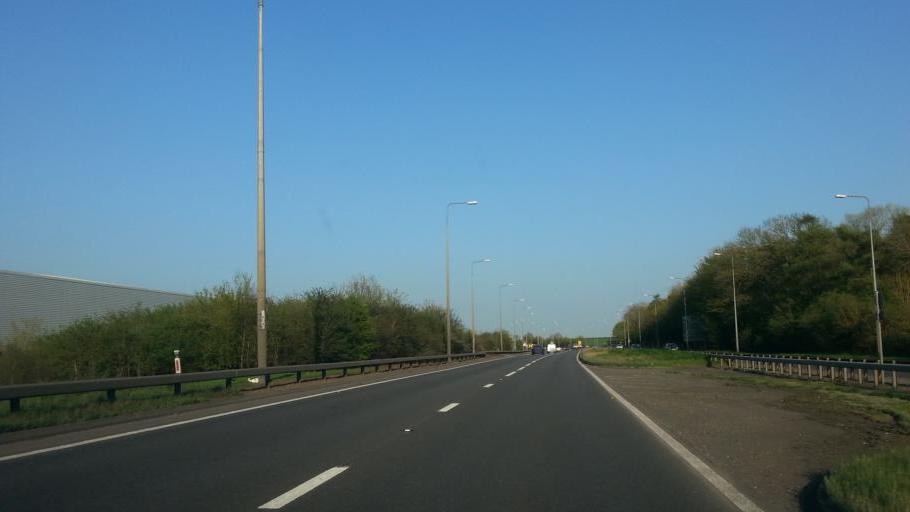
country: GB
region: England
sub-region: Northamptonshire
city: Irchester
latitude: 52.2888
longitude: -0.6666
